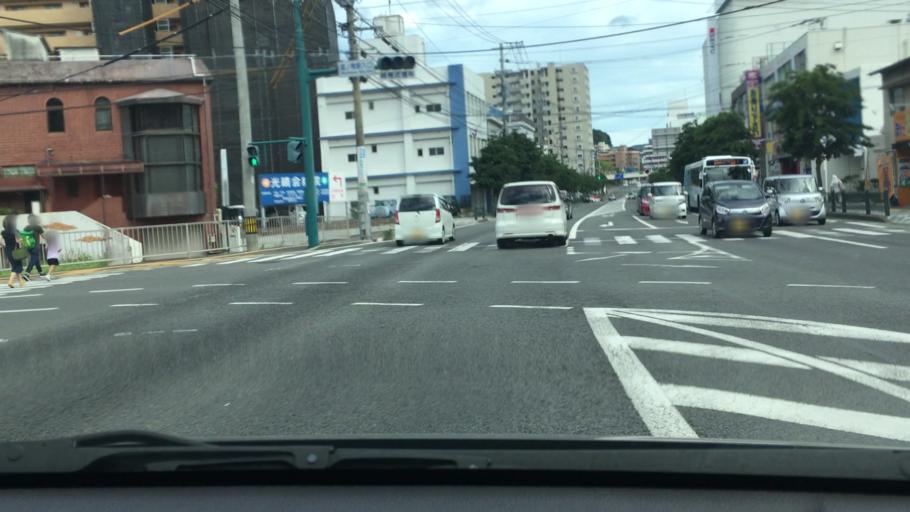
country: JP
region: Nagasaki
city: Togitsu
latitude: 32.8050
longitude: 129.8505
